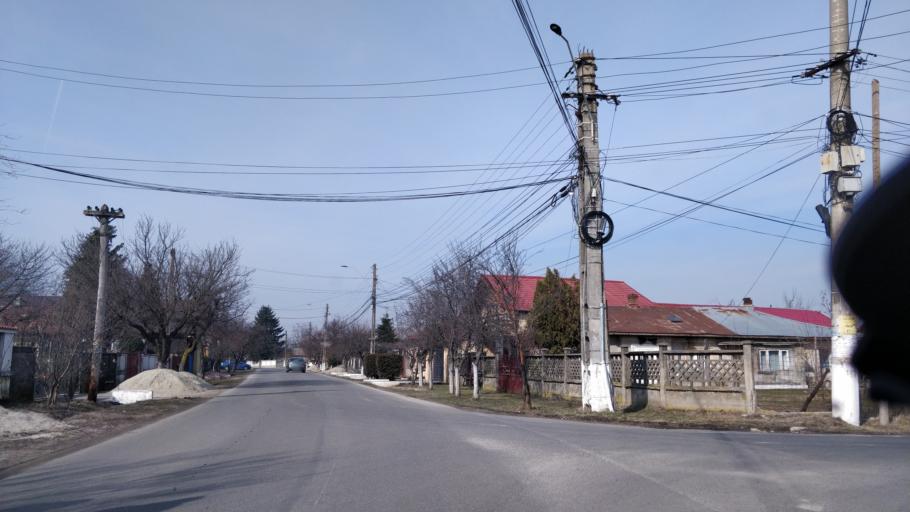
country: RO
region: Giurgiu
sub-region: Comuna Ulmi
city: Ulmi
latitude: 44.4756
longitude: 25.7649
